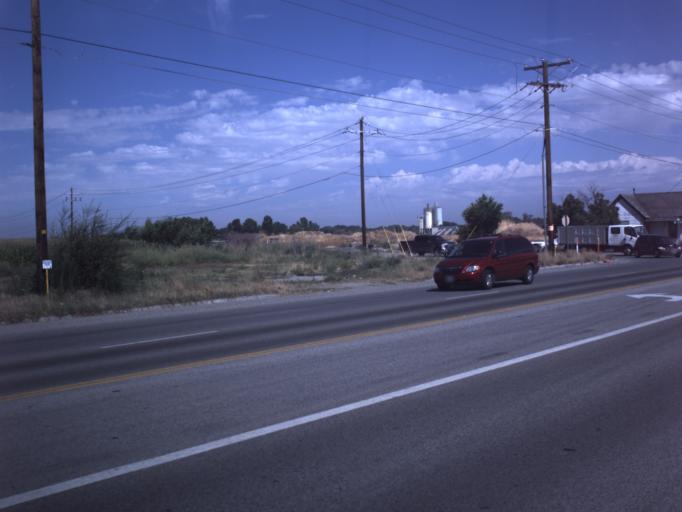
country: US
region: Utah
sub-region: Weber County
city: Marriott-Slaterville
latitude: 41.2327
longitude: -112.0255
